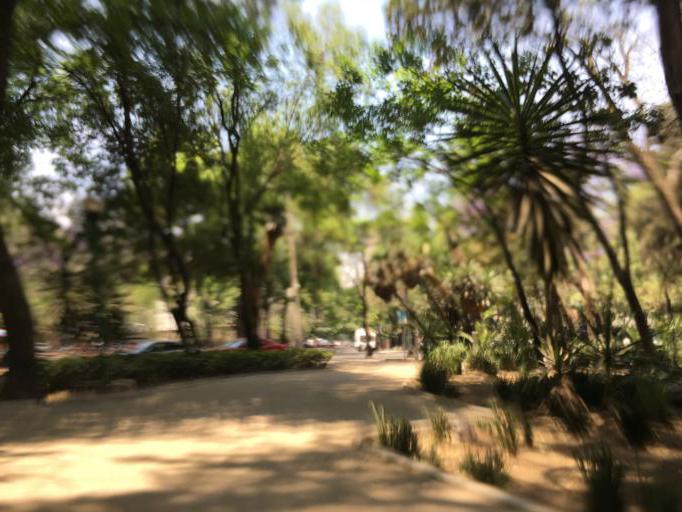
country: MX
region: Mexico City
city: Benito Juarez
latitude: 19.4154
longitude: -99.1715
